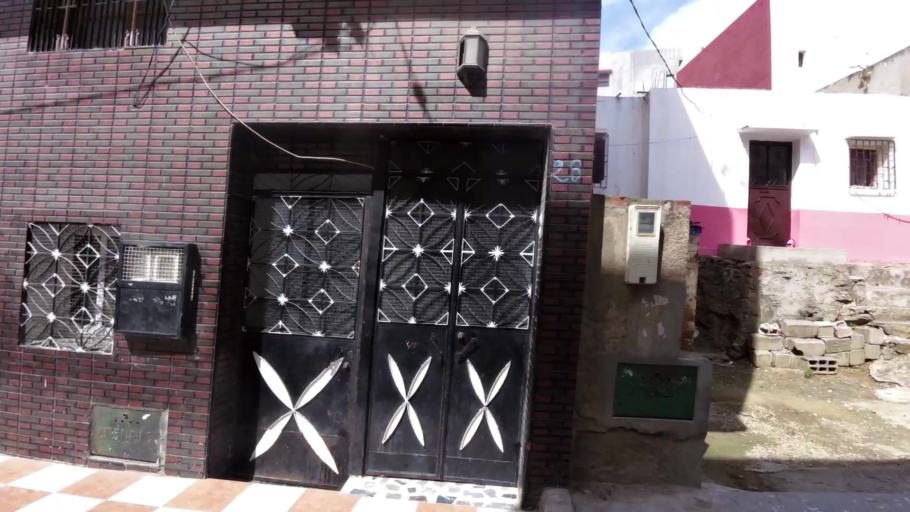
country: MA
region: Tanger-Tetouan
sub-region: Tetouan
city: Martil
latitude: 35.6839
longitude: -5.3333
